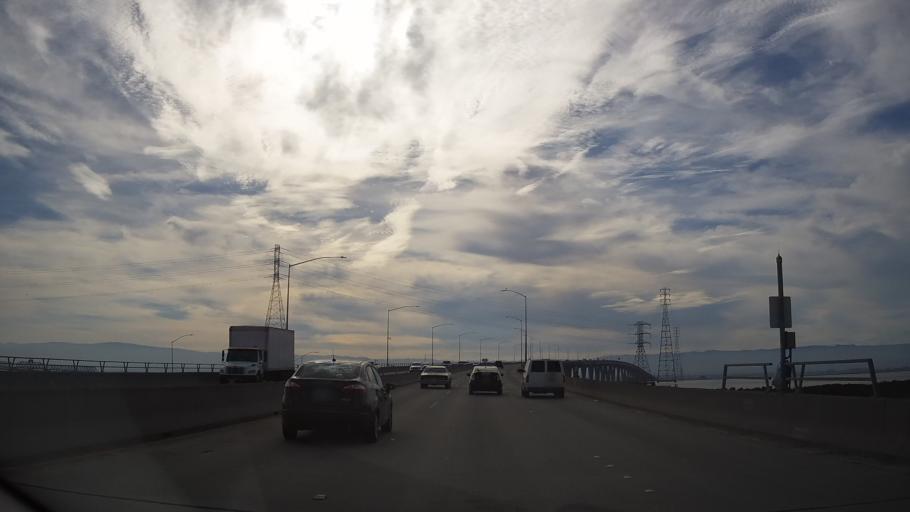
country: US
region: California
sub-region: San Mateo County
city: East Palo Alto
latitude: 37.5139
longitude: -122.1091
